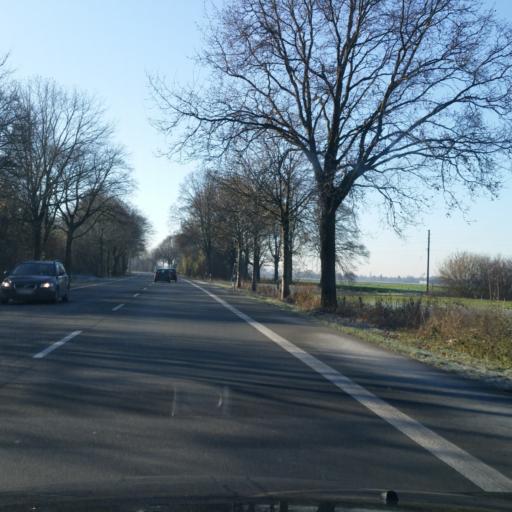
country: DE
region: North Rhine-Westphalia
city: Rees
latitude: 51.7781
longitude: 6.4005
